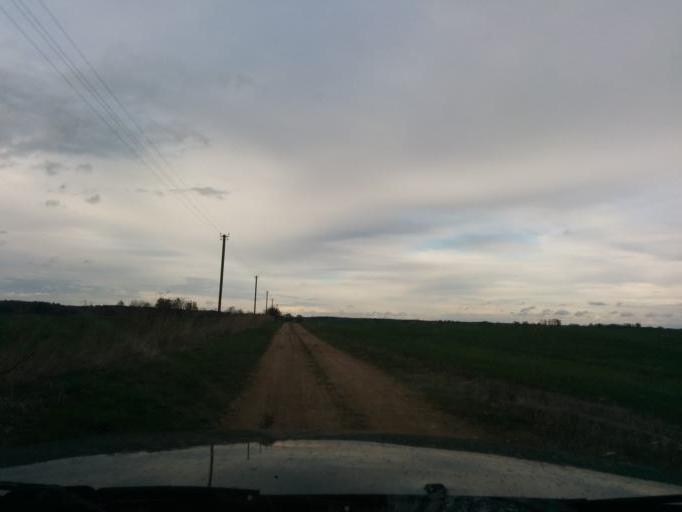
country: LV
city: Tervete
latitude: 56.3675
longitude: 23.5073
